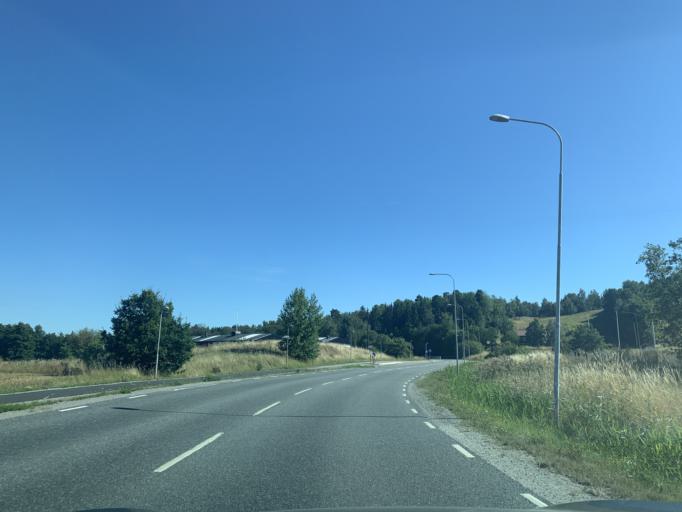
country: SE
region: Stockholm
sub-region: Ekero Kommun
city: Ekeroe
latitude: 59.2824
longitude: 17.8337
